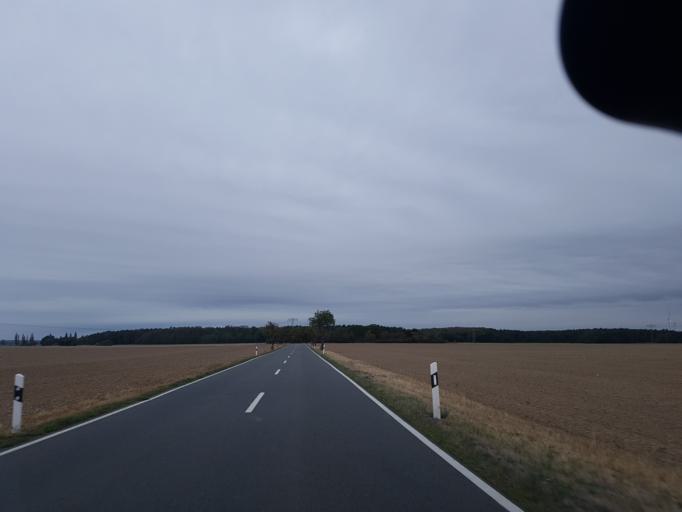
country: DE
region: Saxony-Anhalt
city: Prettin
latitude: 51.6518
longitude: 12.9707
